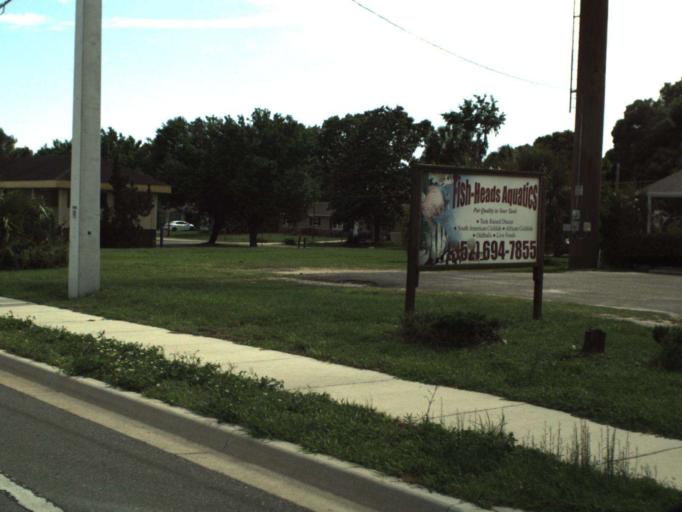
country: US
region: Florida
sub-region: Marion County
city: Silver Springs Shores
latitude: 29.1724
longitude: -82.0538
